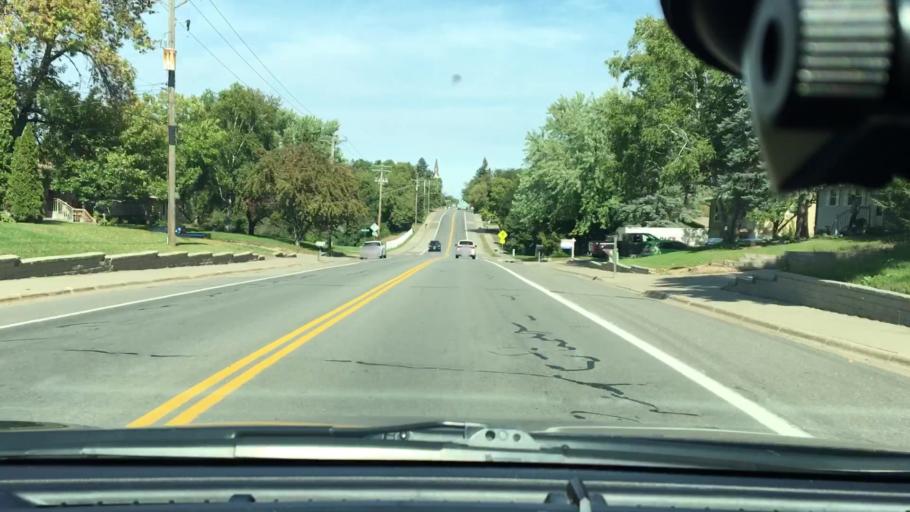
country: US
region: Minnesota
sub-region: Wright County
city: Saint Michael
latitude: 45.2034
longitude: -93.6648
